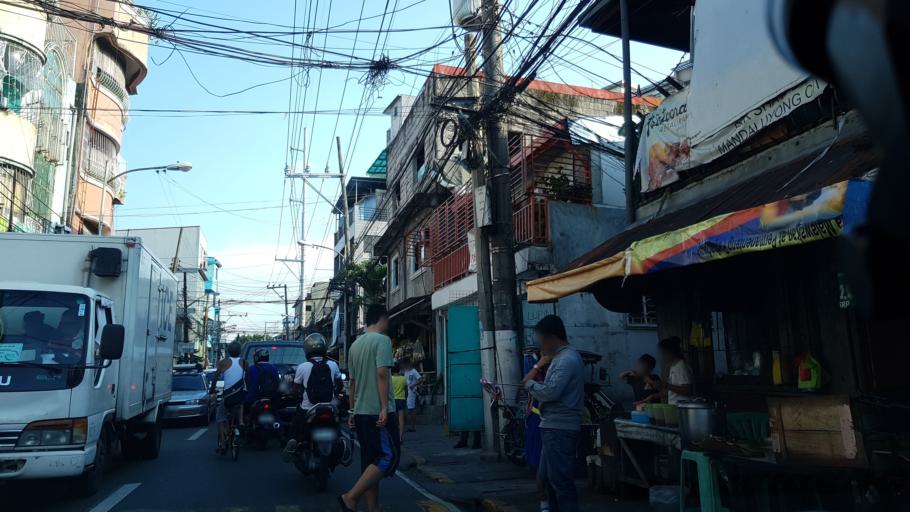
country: PH
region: Metro Manila
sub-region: Mandaluyong
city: Mandaluyong City
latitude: 14.5760
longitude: 121.0274
